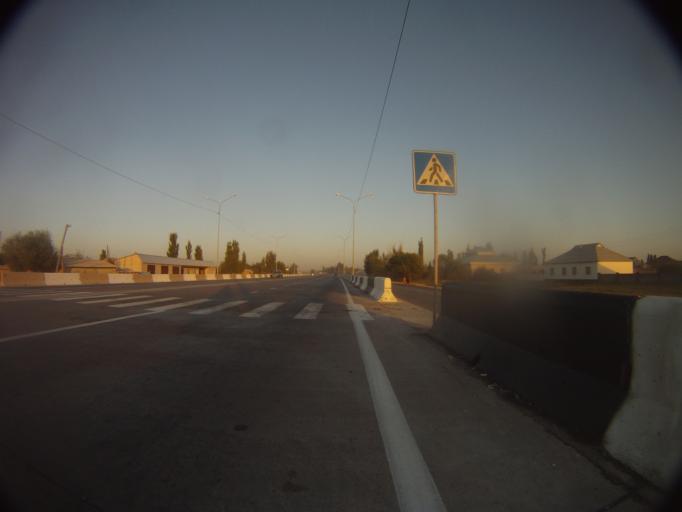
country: KZ
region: Ongtustik Qazaqstan
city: Turkestan
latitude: 43.2626
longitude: 68.3707
